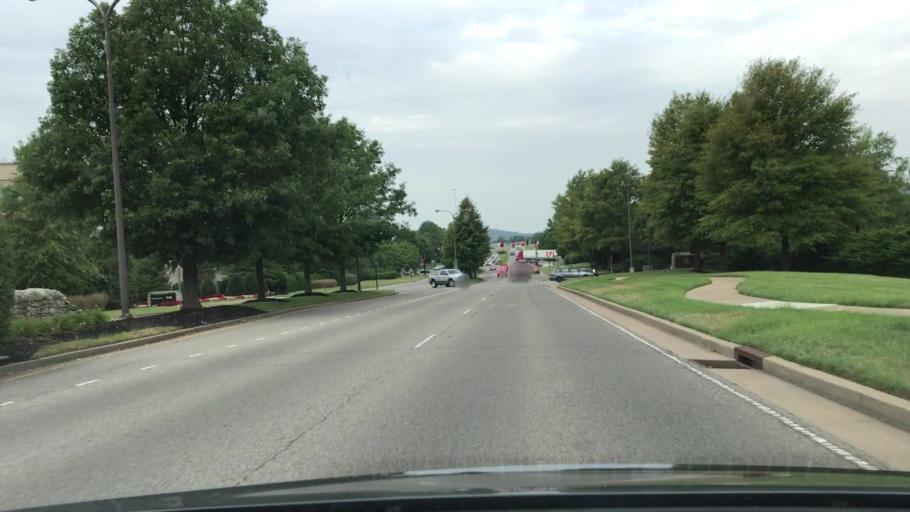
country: US
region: Tennessee
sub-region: Williamson County
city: Franklin
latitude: 35.9457
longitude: -86.8059
